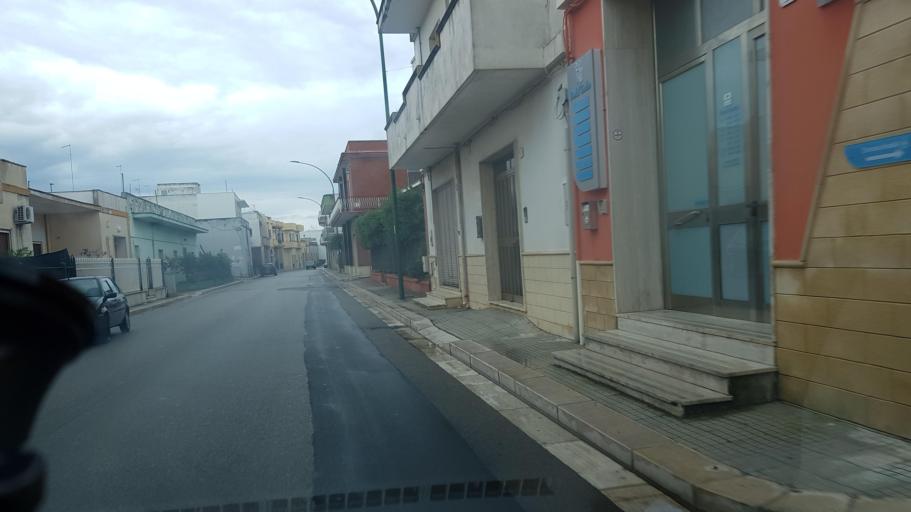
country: IT
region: Apulia
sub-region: Provincia di Lecce
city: Guagnano
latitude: 40.3974
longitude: 17.9534
